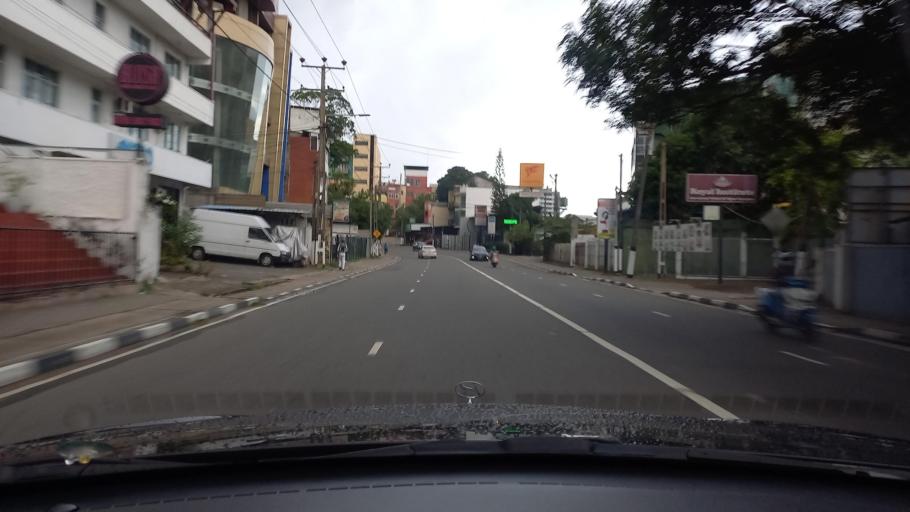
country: LK
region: Western
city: Sri Jayewardenepura Kotte
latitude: 6.8756
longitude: 79.8941
